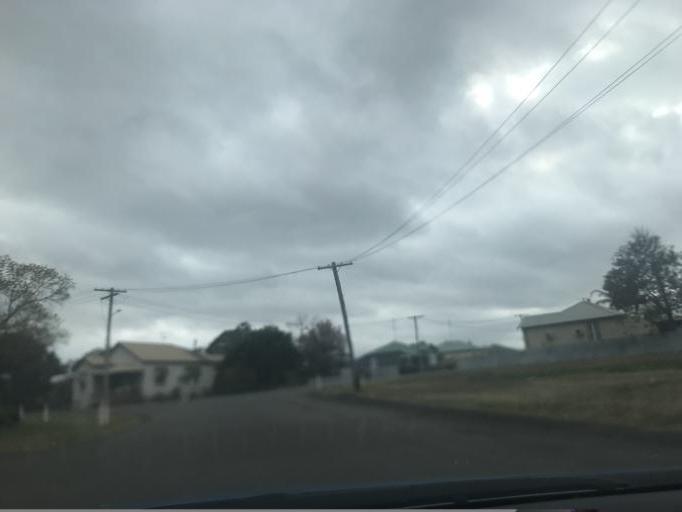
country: AU
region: New South Wales
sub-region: Cessnock
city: Cessnock
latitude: -32.9028
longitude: 151.2831
